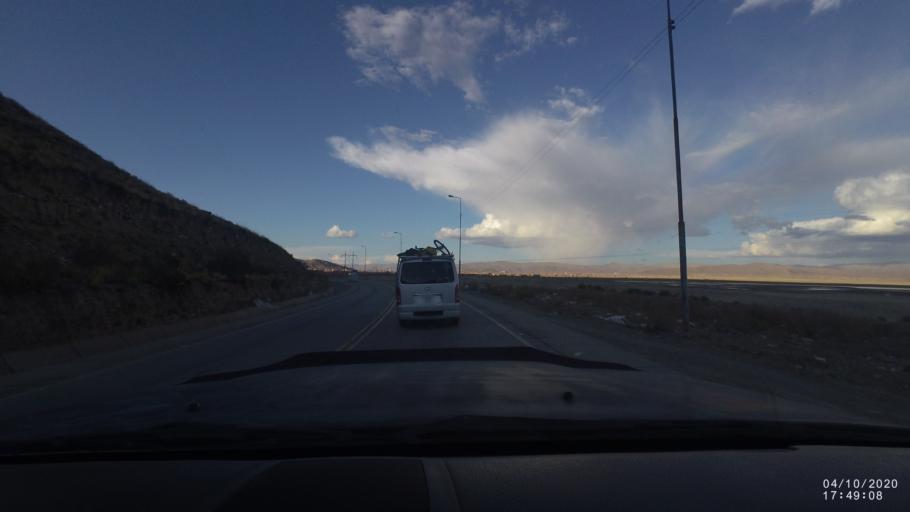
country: BO
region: Oruro
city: Oruro
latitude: -18.0136
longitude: -67.1378
